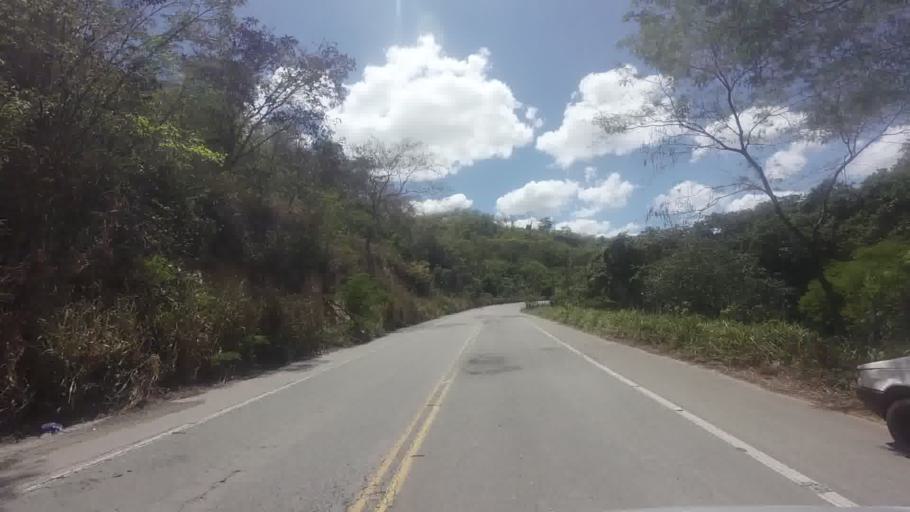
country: BR
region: Rio de Janeiro
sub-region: Santo Antonio De Padua
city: Santo Antonio de Padua
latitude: -21.6581
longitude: -42.3093
